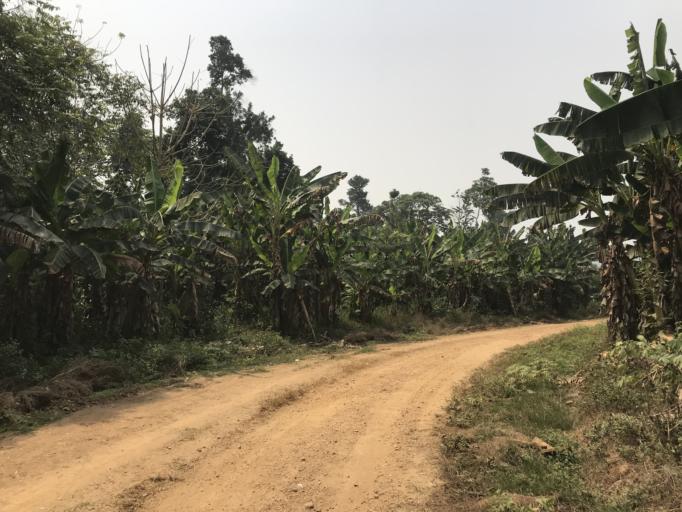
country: NG
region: Osun
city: Ifetedo
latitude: 7.0266
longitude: 4.4759
